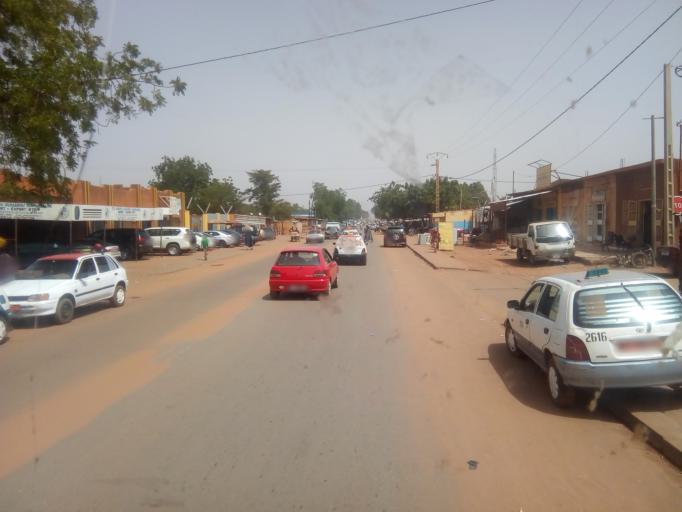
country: NE
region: Niamey
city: Niamey
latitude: 13.5273
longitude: 2.1215
